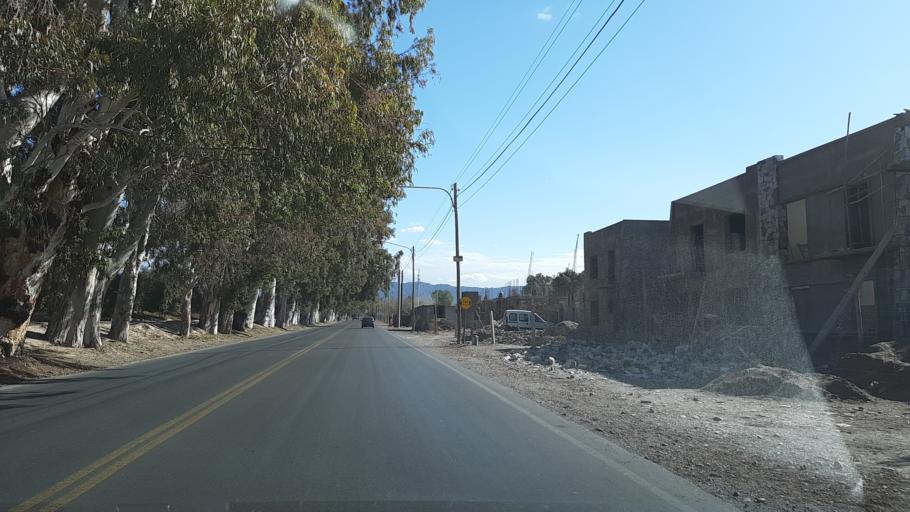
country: AR
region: San Juan
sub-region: Departamento de Rivadavia
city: Rivadavia
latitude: -31.5388
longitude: -68.5977
